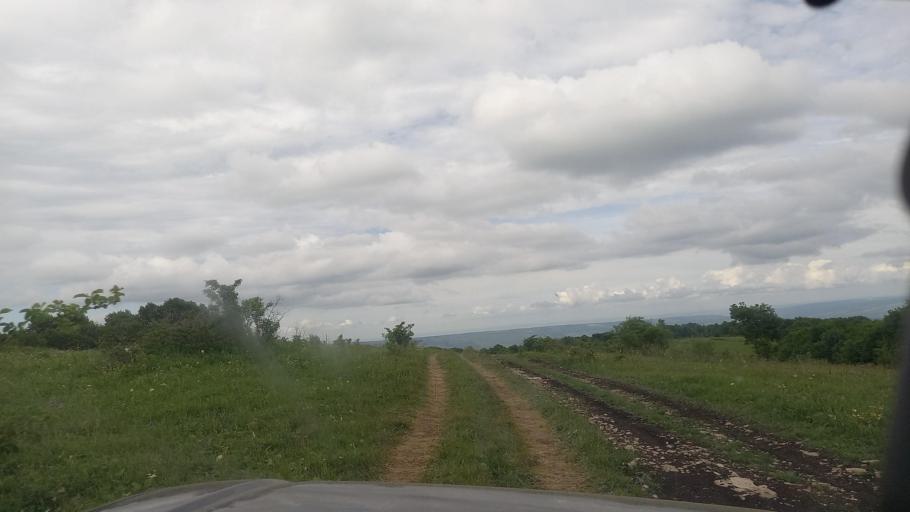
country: RU
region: Karachayevo-Cherkesiya
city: Pregradnaya
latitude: 44.0173
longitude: 41.2822
